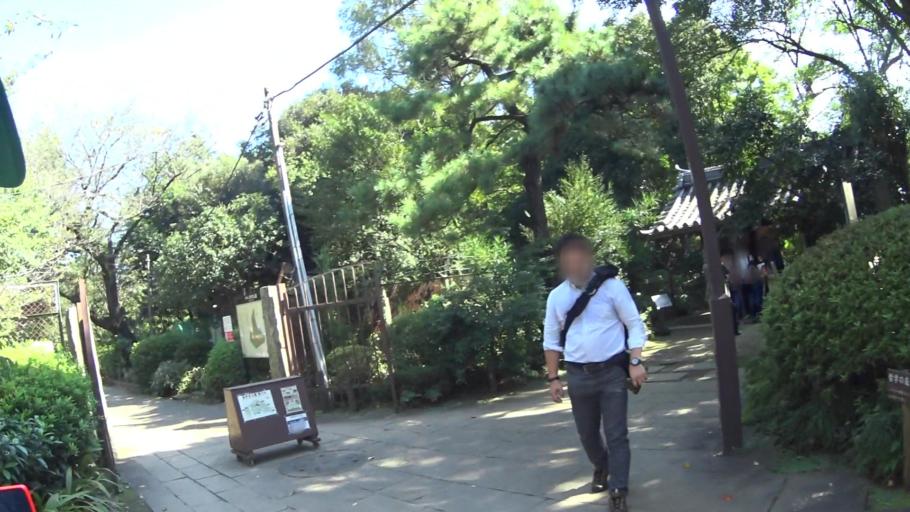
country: JP
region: Tokyo
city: Tokyo
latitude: 35.7224
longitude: 139.6743
